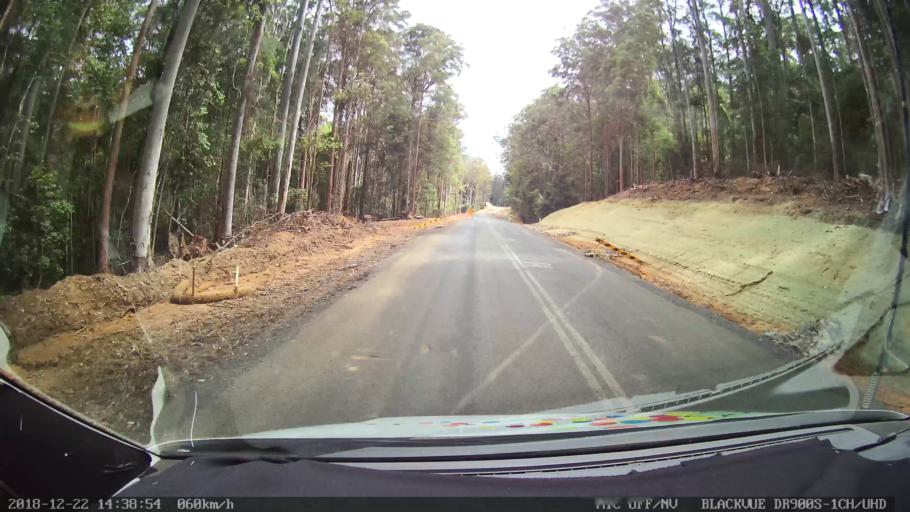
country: AU
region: New South Wales
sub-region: Bellingen
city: Dorrigo
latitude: -30.1419
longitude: 152.5950
